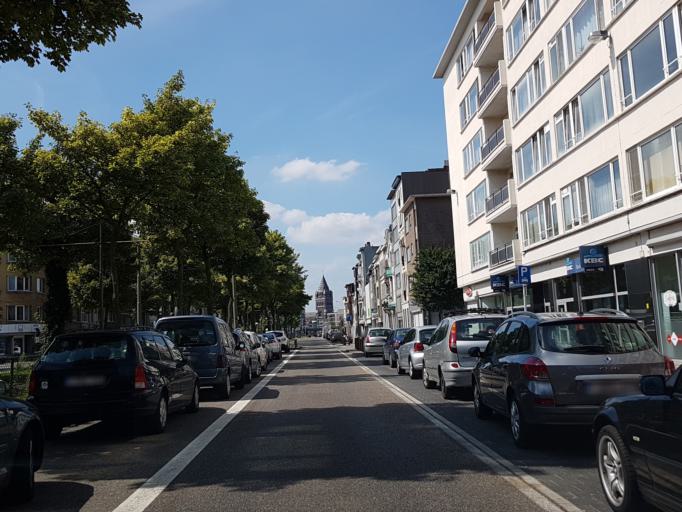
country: BE
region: Flanders
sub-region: Provincie Antwerpen
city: Borsbeek
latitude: 51.2113
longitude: 4.4513
